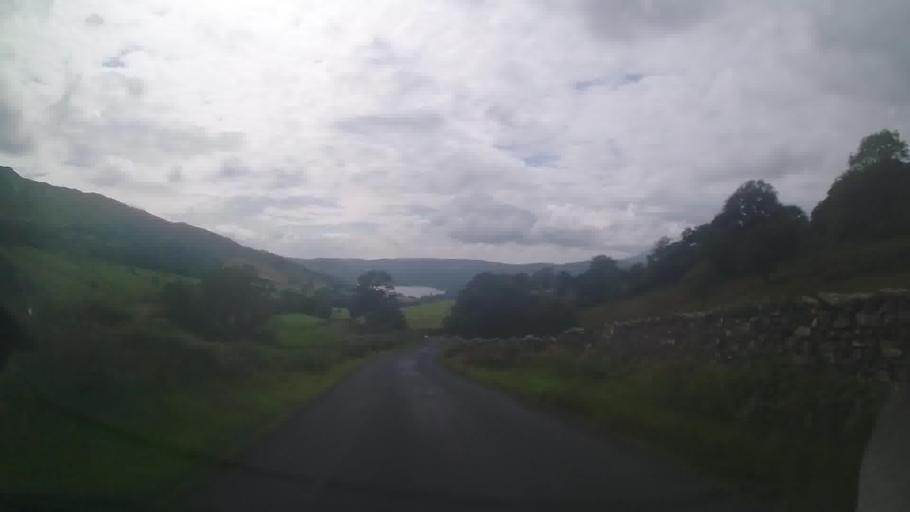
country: GB
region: England
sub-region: Cumbria
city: Ambleside
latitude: 54.4428
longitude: -2.9444
